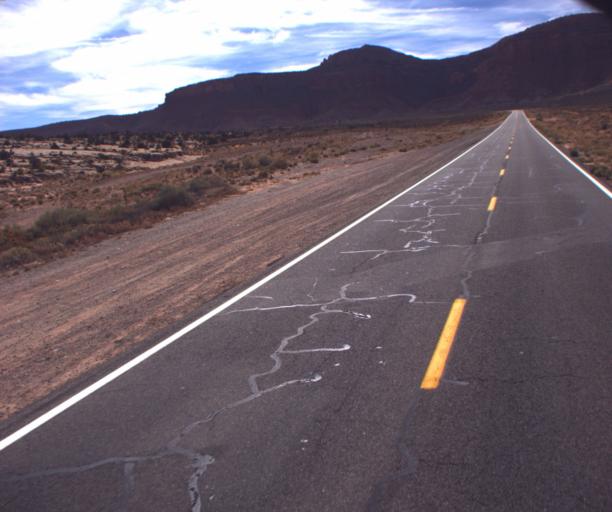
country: US
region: Arizona
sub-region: Navajo County
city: Kayenta
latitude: 36.8594
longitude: -110.2675
